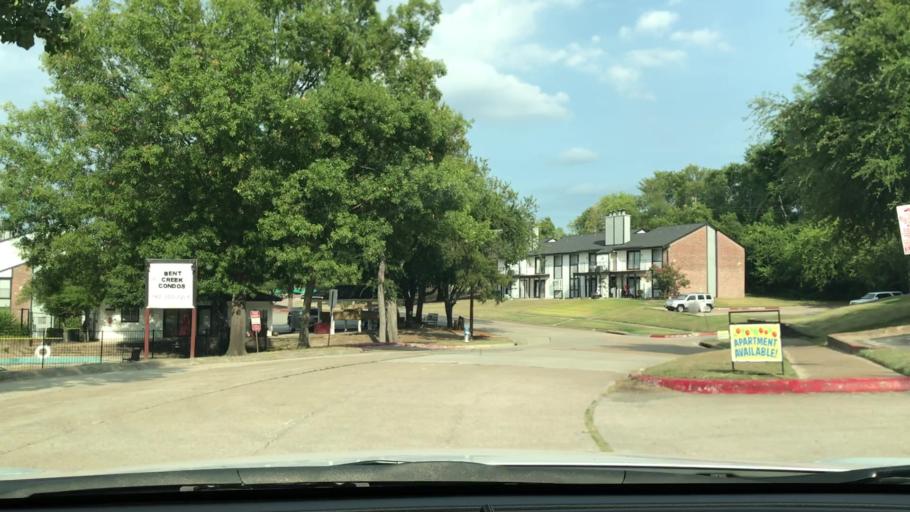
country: US
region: Texas
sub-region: Rockwall County
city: Rockwall
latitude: 32.9274
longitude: -96.4632
